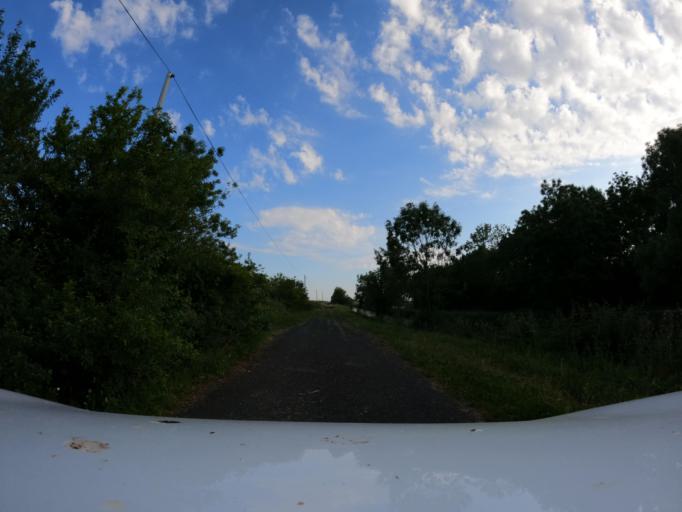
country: FR
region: Pays de la Loire
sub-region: Departement de la Vendee
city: Champagne-les-Marais
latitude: 46.3792
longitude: -1.0912
